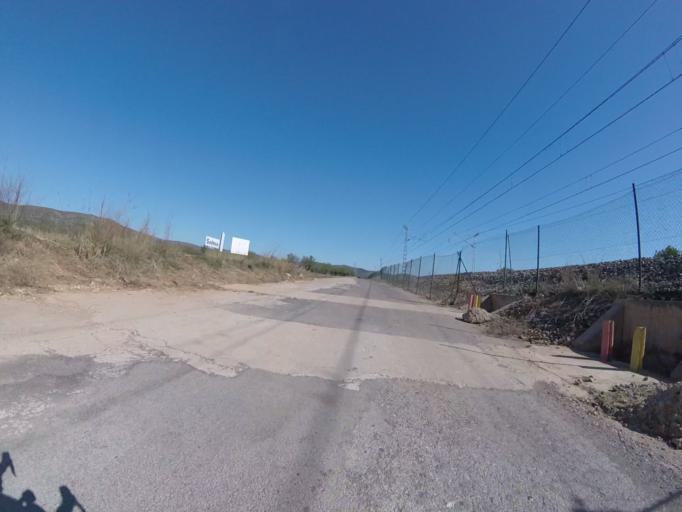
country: ES
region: Valencia
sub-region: Provincia de Castello
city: Alcala de Xivert
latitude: 40.3138
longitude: 0.2323
